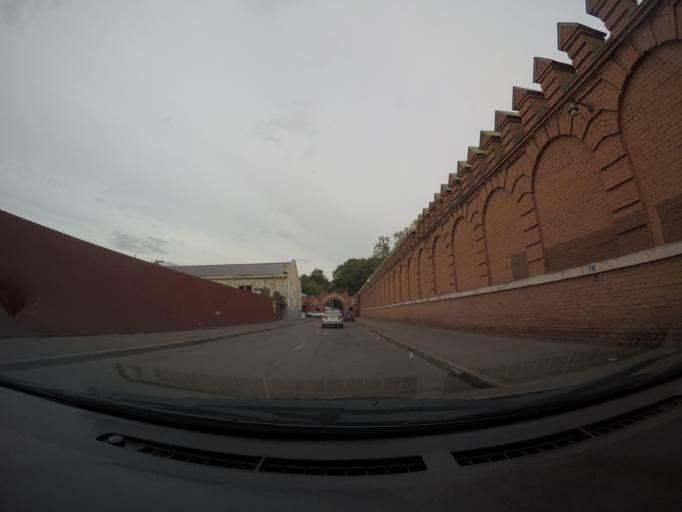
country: RU
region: Moskovskaya
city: Bogorodskoye
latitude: 55.7918
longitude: 37.7183
